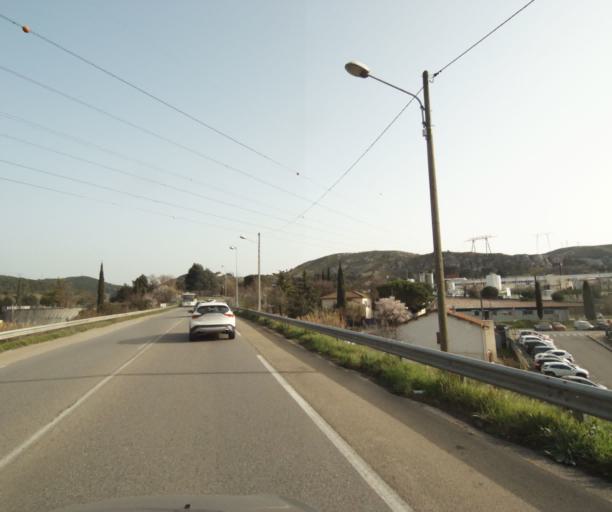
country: FR
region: Provence-Alpes-Cote d'Azur
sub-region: Departement des Bouches-du-Rhone
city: Les Pennes-Mirabeau
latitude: 43.4105
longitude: 5.3233
